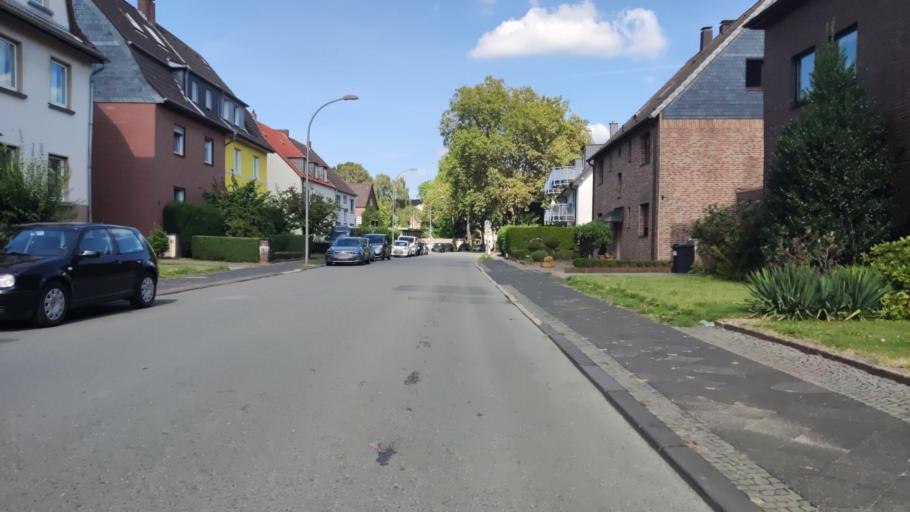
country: DE
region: North Rhine-Westphalia
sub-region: Regierungsbezirk Arnsberg
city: Bochum
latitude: 51.4667
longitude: 7.2372
